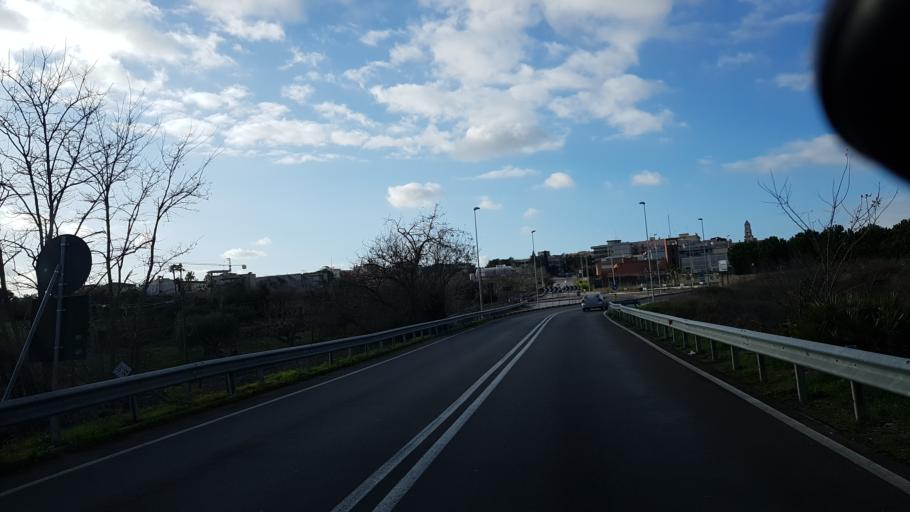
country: IT
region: Apulia
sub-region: Provincia di Bari
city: Putignano
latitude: 40.8457
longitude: 17.1331
